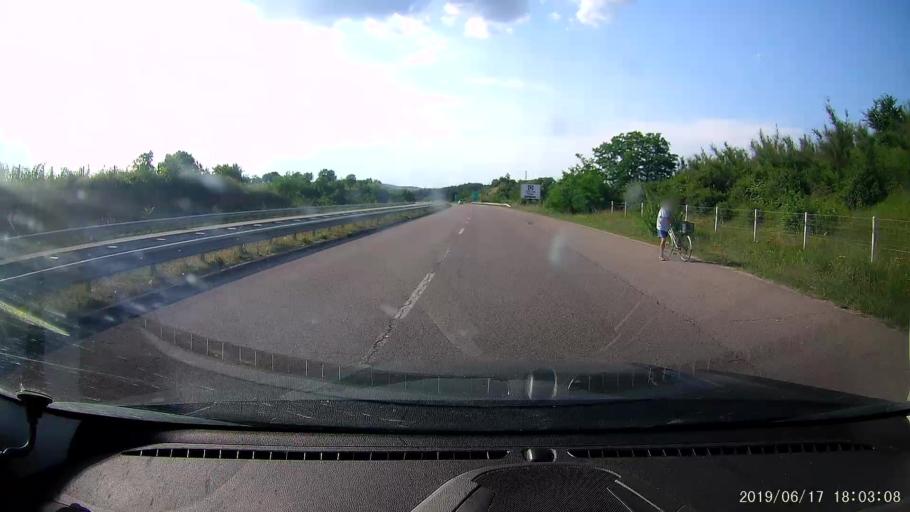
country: BG
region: Khaskovo
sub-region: Obshtina Svilengrad
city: Svilengrad
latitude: 41.7727
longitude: 26.2240
